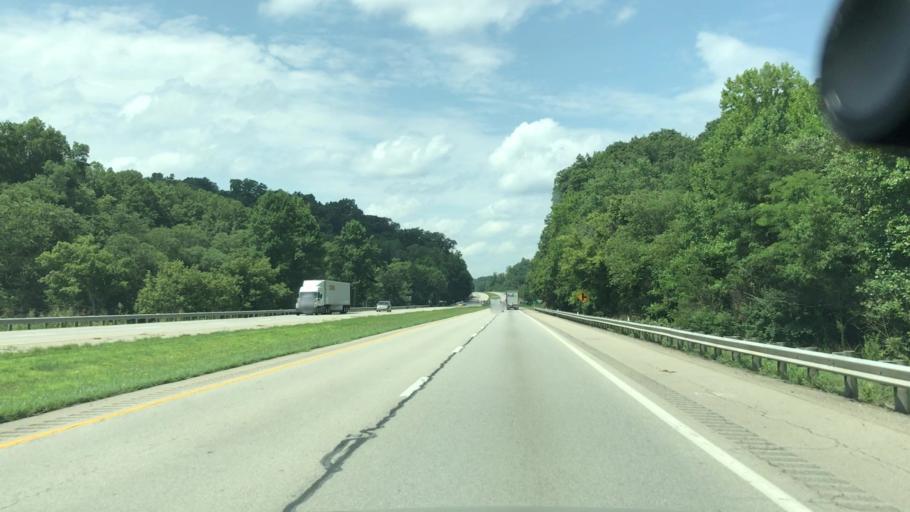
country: US
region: Ohio
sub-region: Jackson County
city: Jackson
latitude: 39.1005
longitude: -82.6691
